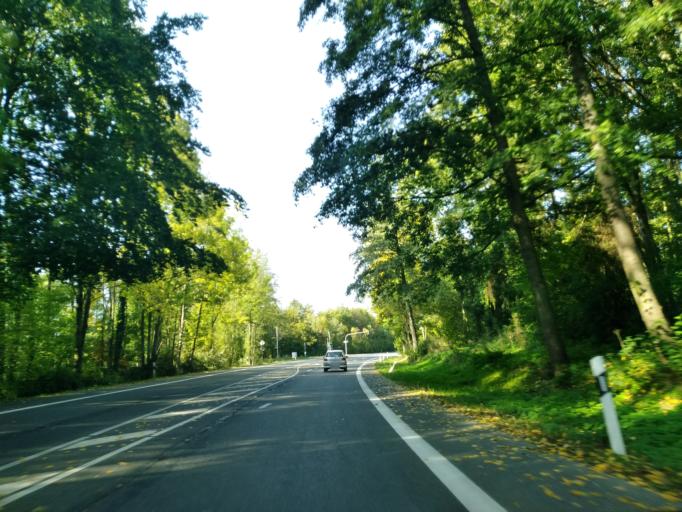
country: DE
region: North Rhine-Westphalia
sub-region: Regierungsbezirk Koln
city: Hennef
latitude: 50.7128
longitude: 7.2798
